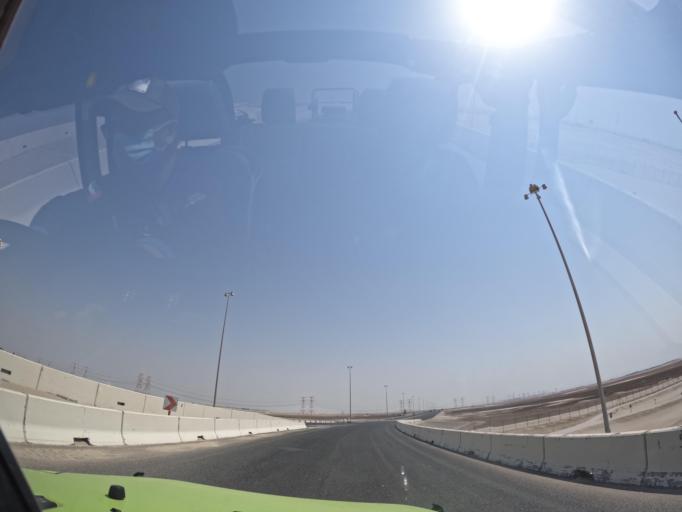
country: AE
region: Abu Dhabi
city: Abu Dhabi
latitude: 24.2112
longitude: 54.4154
